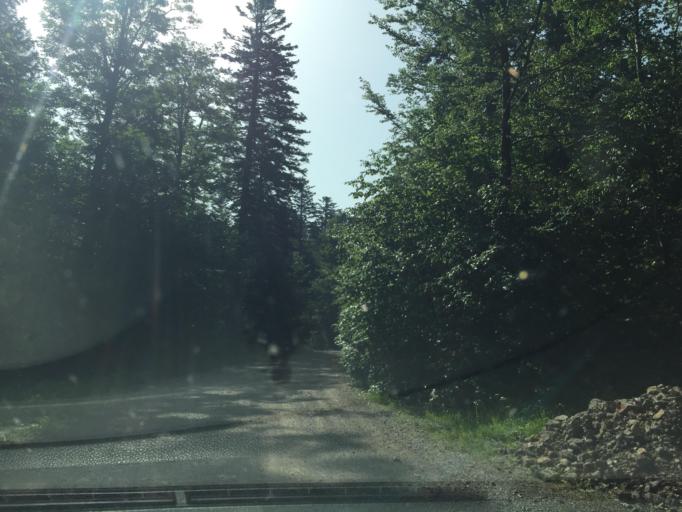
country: HR
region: Primorsko-Goranska
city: Podhum
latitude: 45.4422
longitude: 14.5591
